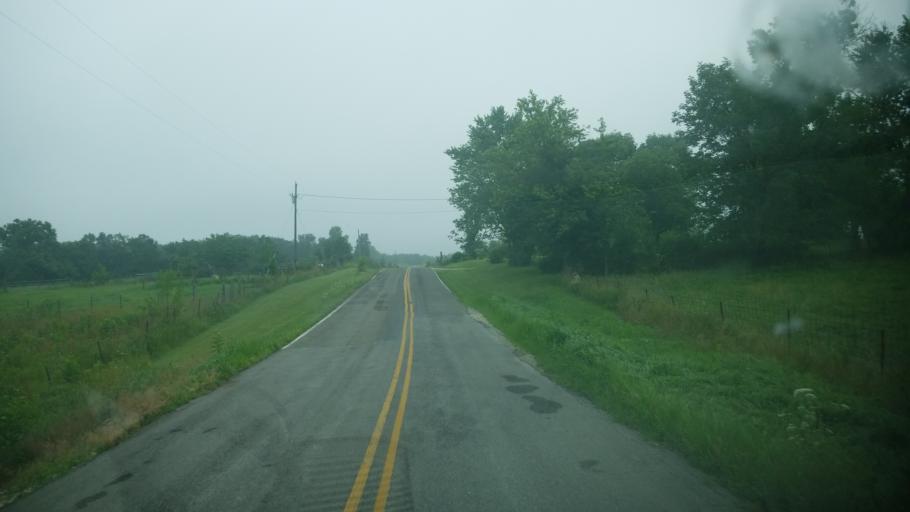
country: US
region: Missouri
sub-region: Audrain County
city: Vandalia
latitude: 39.2807
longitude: -91.3463
